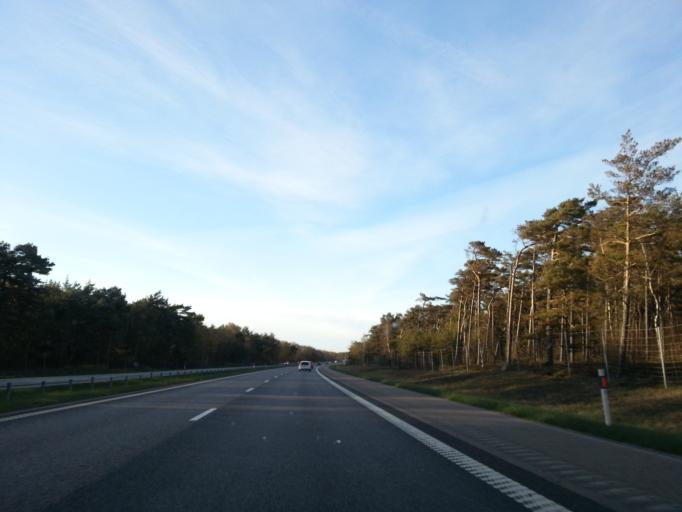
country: SE
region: Halland
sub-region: Halmstads Kommun
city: Paarp
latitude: 56.5712
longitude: 12.9489
